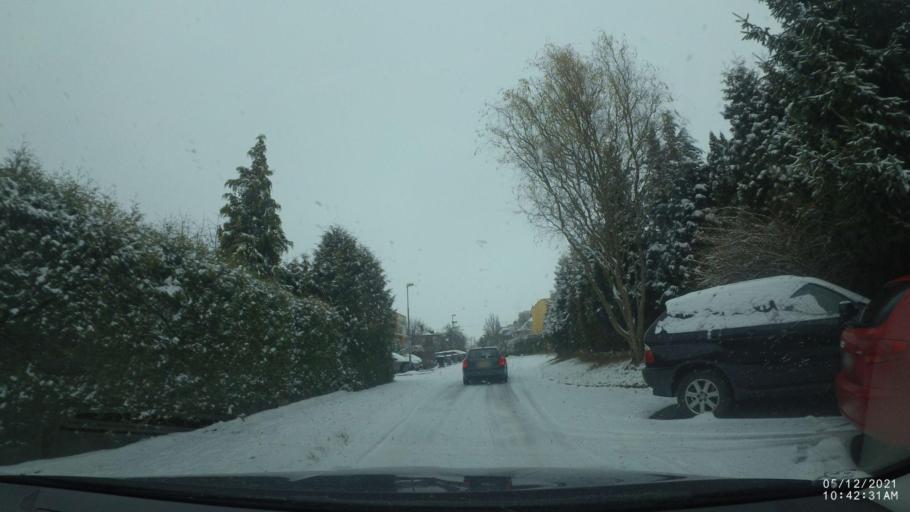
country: CZ
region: Kralovehradecky
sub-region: Okres Rychnov nad Kneznou
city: Rychnov nad Kneznou
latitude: 50.1666
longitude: 16.2852
